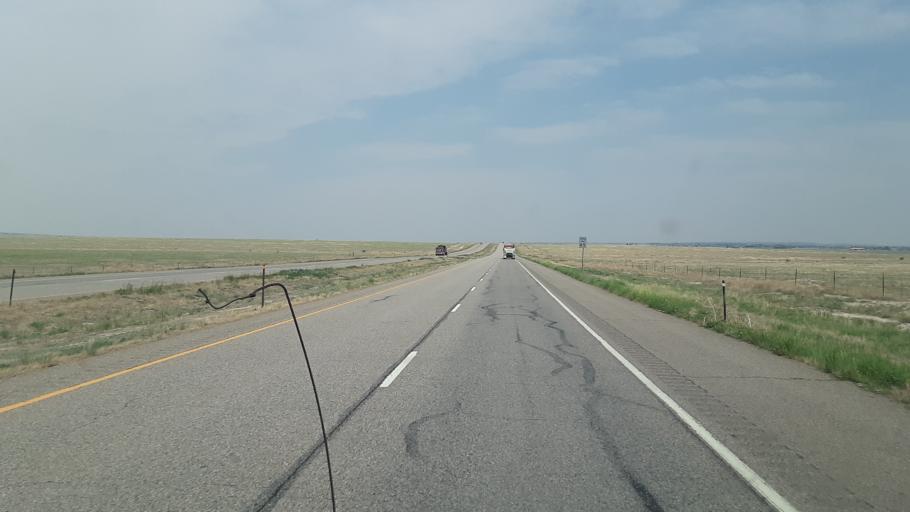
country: US
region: Colorado
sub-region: Pueblo County
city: Pueblo West
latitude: 38.3589
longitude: -104.8637
